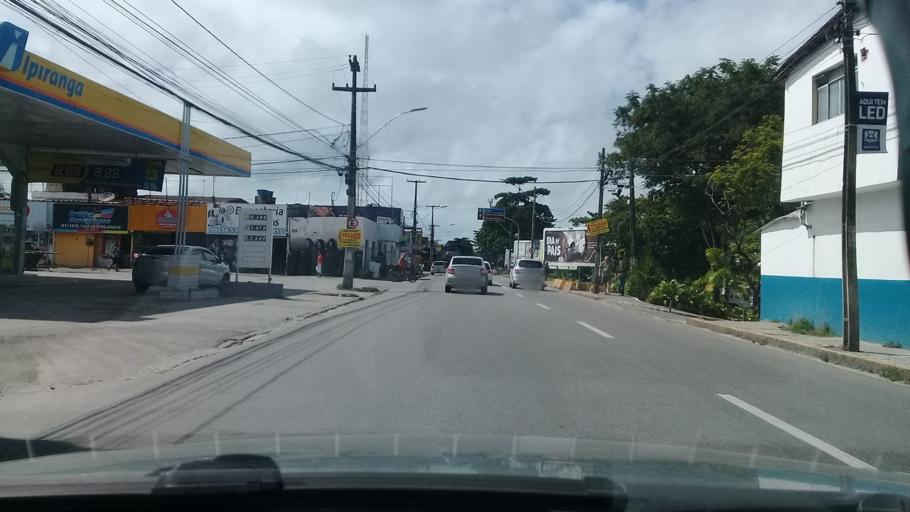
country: BR
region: Pernambuco
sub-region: Jaboatao Dos Guararapes
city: Jaboatao
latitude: -8.1639
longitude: -34.9225
